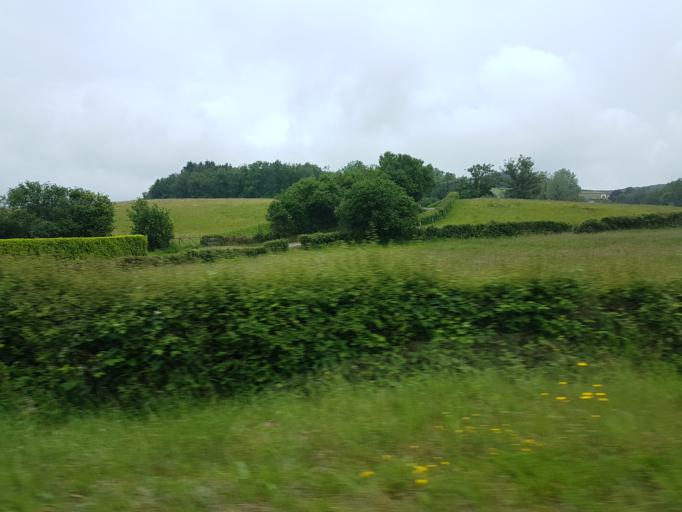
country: FR
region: Bourgogne
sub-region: Departement de la Nievre
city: Chateau-Chinon(Ville)
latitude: 47.0498
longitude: 3.9608
